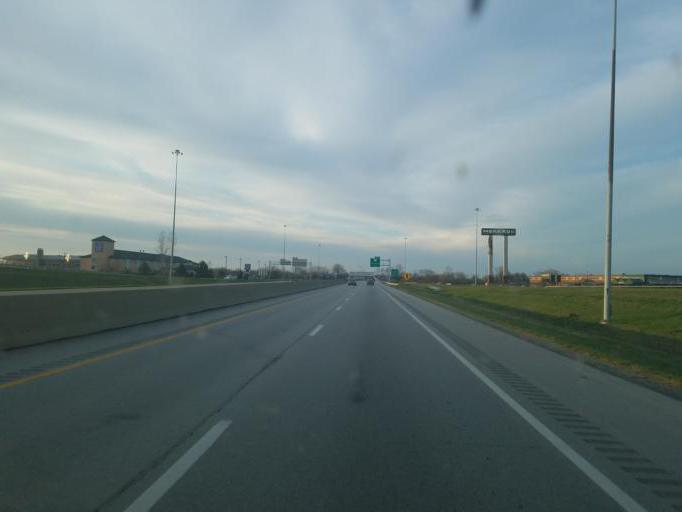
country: US
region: Ohio
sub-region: Wood County
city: Northwood
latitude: 41.6169
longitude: -83.4769
